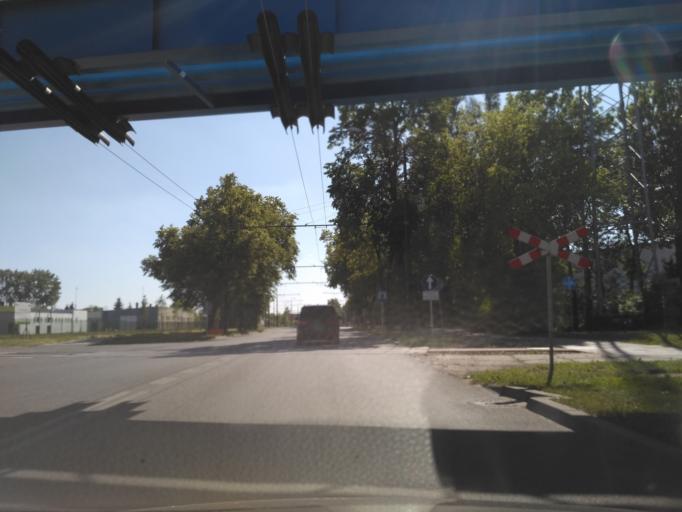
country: PL
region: Lublin Voivodeship
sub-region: Powiat lubelski
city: Lublin
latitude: 51.2046
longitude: 22.5628
